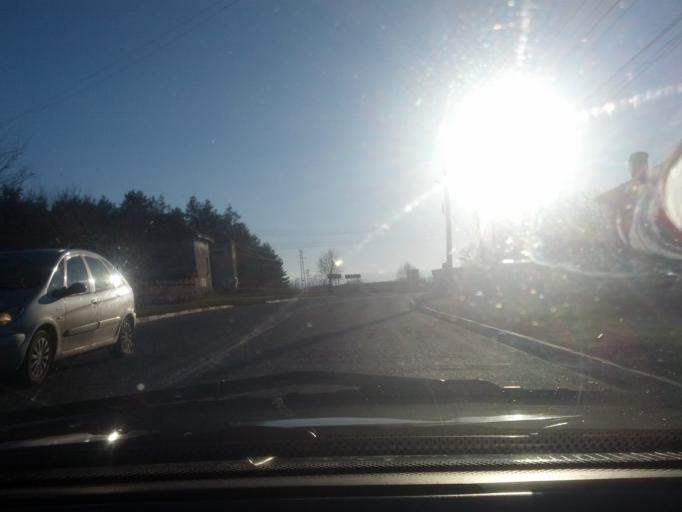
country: BG
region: Vratsa
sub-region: Obshtina Borovan
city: Borovan
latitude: 43.4299
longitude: 23.7637
